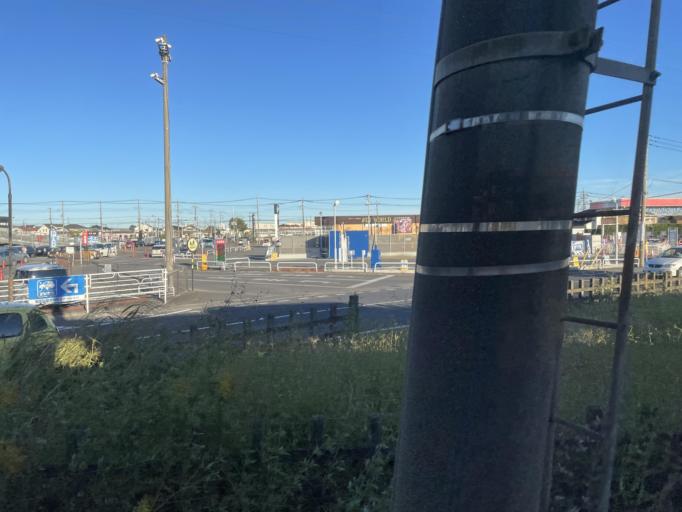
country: JP
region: Saitama
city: Satte
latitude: 36.0602
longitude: 139.7136
